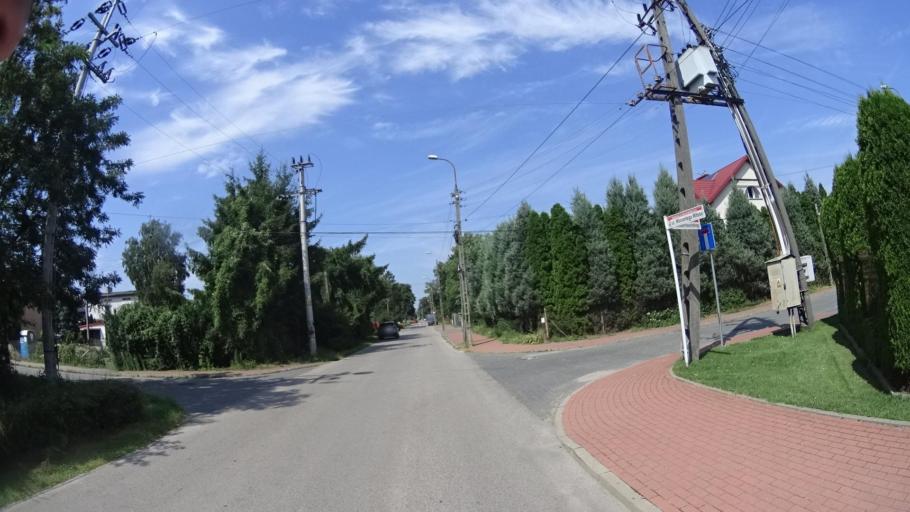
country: PL
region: Masovian Voivodeship
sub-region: Powiat warszawski zachodni
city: Ozarow Mazowiecki
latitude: 52.2055
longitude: 20.7942
